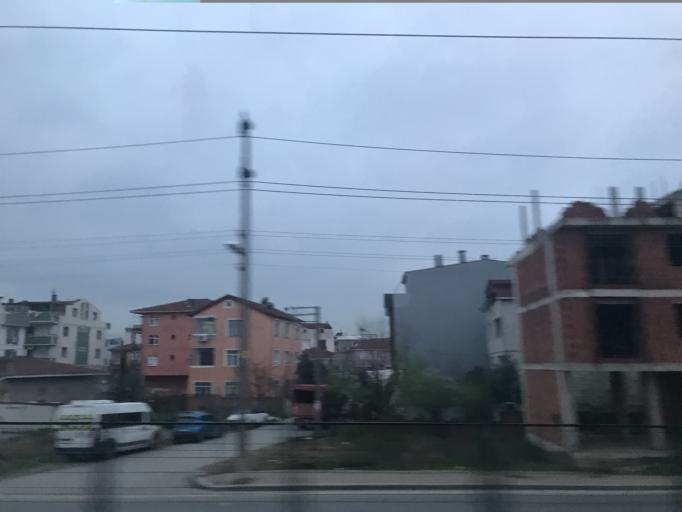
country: TR
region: Kocaeli
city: Darica
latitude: 40.7884
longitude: 29.3964
